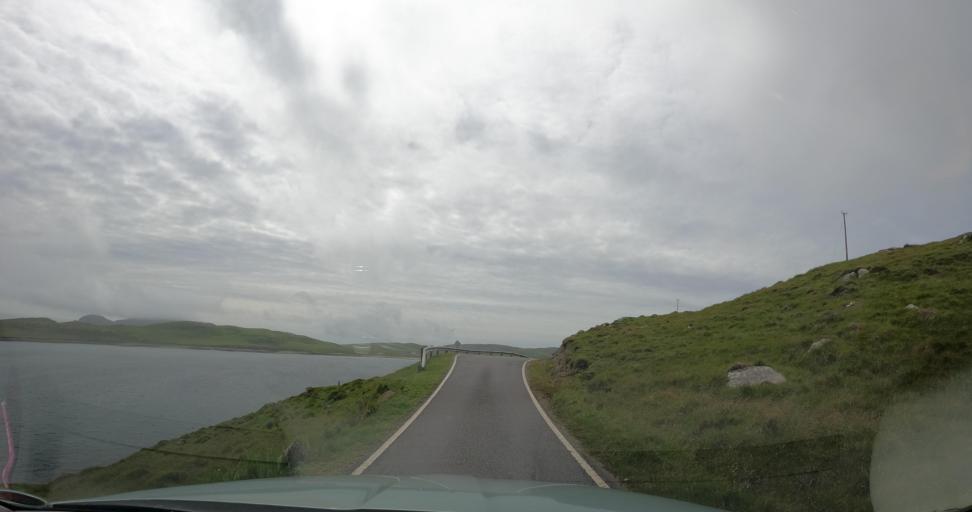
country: GB
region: Scotland
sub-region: Eilean Siar
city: Barra
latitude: 56.9301
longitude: -7.5250
